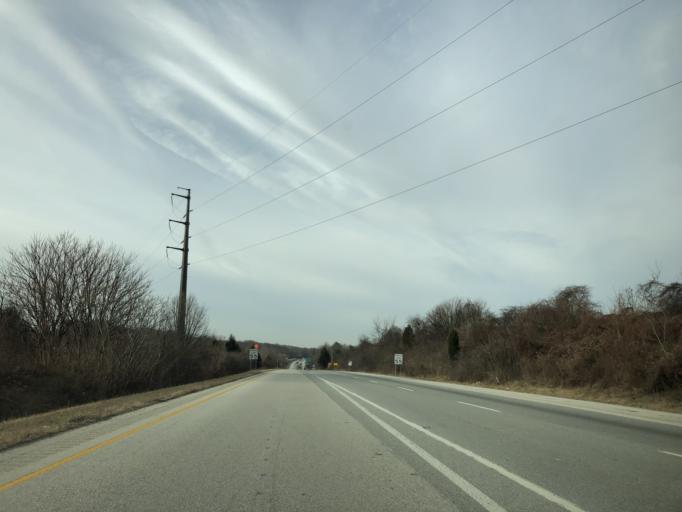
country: US
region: Pennsylvania
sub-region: Chester County
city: Exton
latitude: 40.0295
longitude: -75.5920
